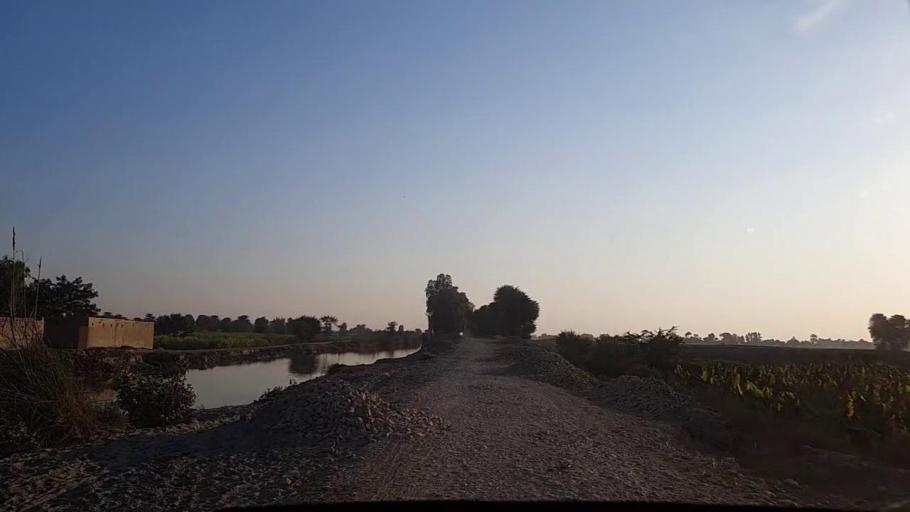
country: PK
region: Sindh
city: Sobhadero
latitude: 27.3851
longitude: 68.3821
